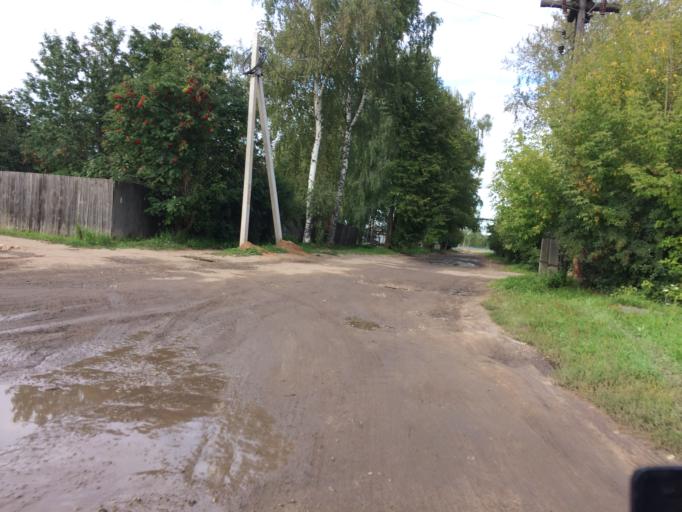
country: RU
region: Mariy-El
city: Yoshkar-Ola
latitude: 56.6586
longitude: 48.0090
